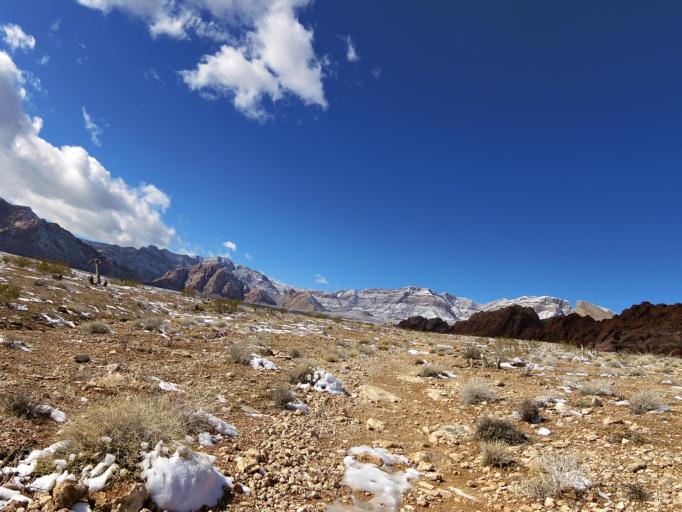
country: US
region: Nevada
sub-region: Clark County
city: Summerlin South
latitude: 36.1419
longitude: -115.4264
